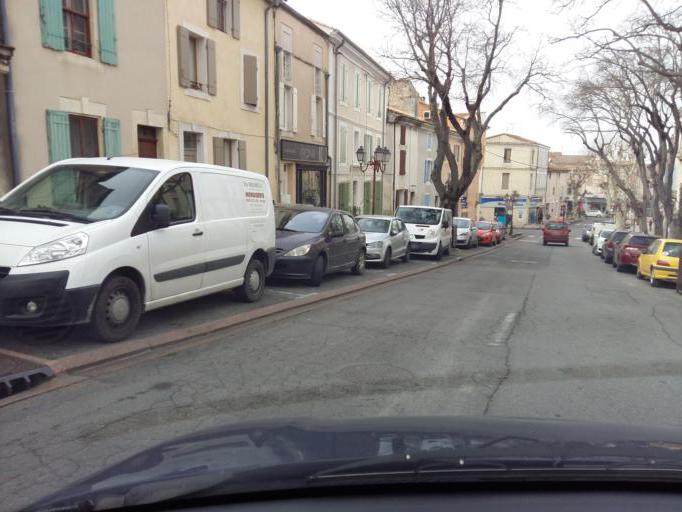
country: FR
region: Provence-Alpes-Cote d'Azur
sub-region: Departement des Bouches-du-Rhone
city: Chateaurenard
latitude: 43.8818
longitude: 4.8556
